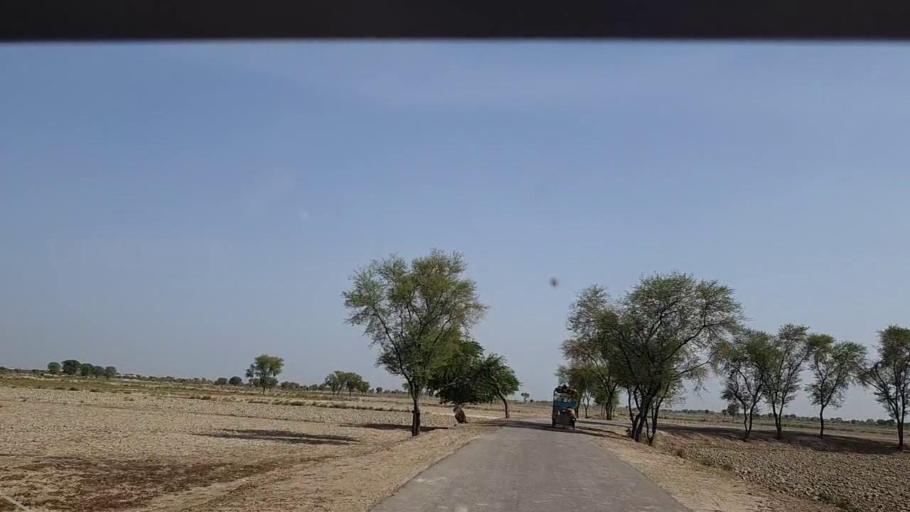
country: PK
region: Sindh
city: Phulji
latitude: 26.9227
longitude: 67.6787
